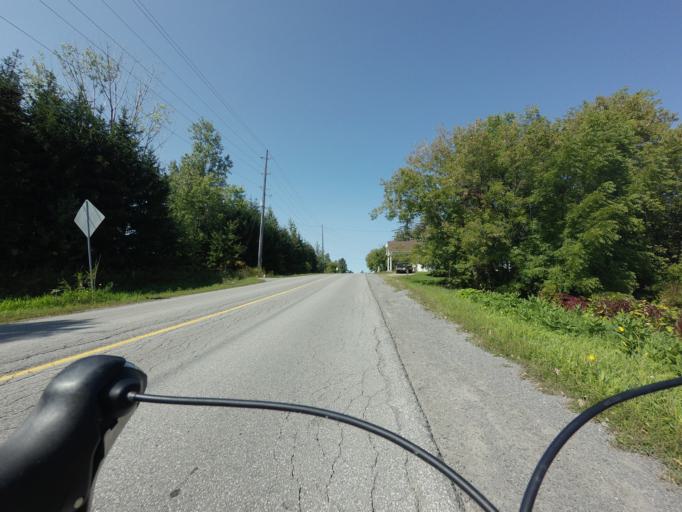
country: CA
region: Ontario
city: Arnprior
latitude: 45.4552
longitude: -76.0904
